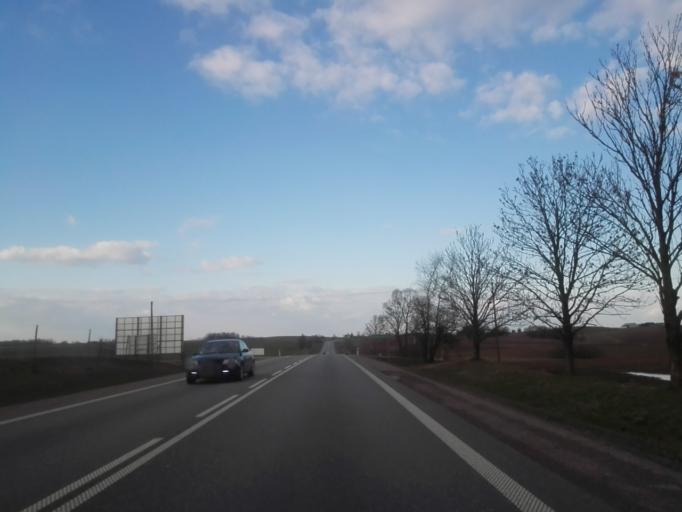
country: PL
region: Podlasie
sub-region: Suwalki
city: Suwalki
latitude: 54.2019
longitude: 23.0216
